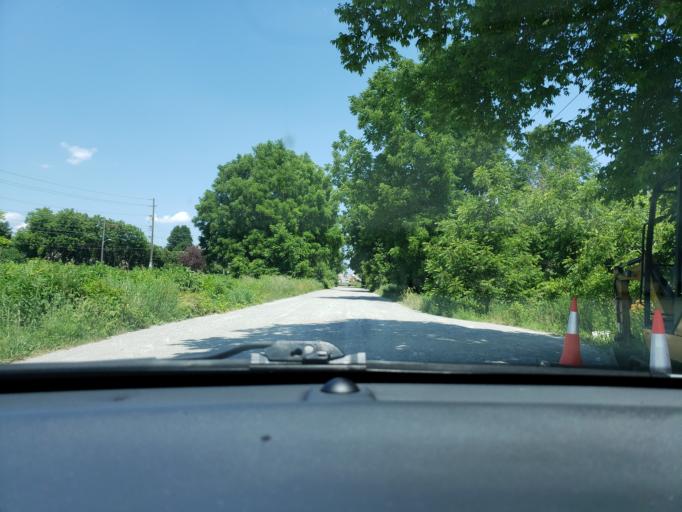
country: CA
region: Ontario
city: Newmarket
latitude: 44.0696
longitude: -79.4582
